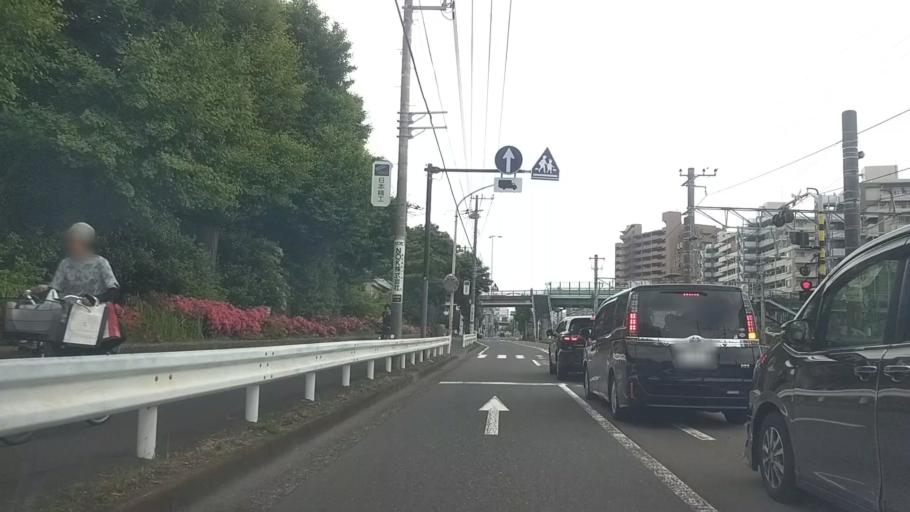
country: JP
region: Kanagawa
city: Fujisawa
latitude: 35.3385
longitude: 139.4755
